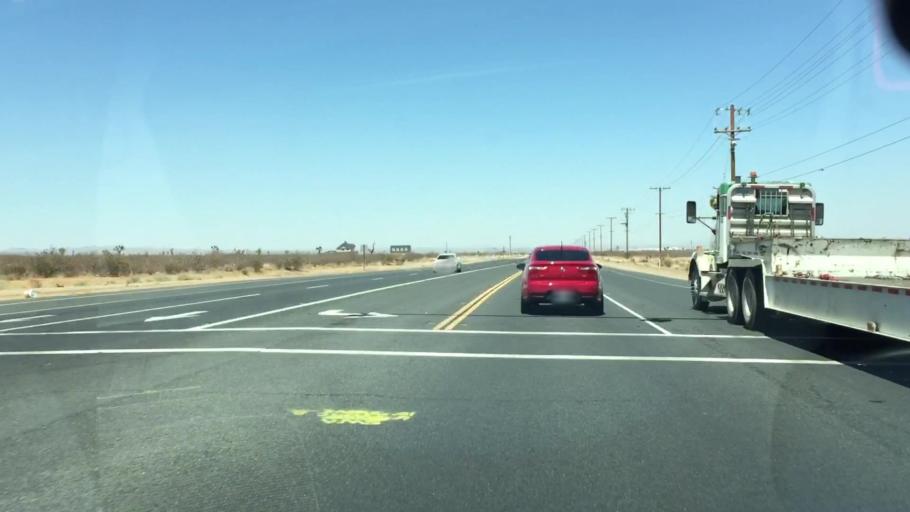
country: US
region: California
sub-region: San Bernardino County
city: Mountain View Acres
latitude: 34.4560
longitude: -117.3996
